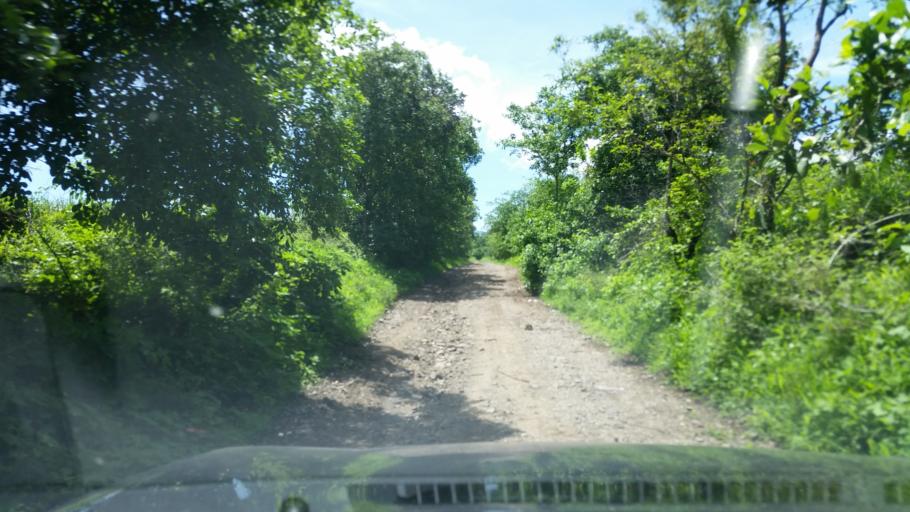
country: NI
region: Chinandega
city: Puerto Morazan
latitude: 12.7607
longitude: -87.1265
